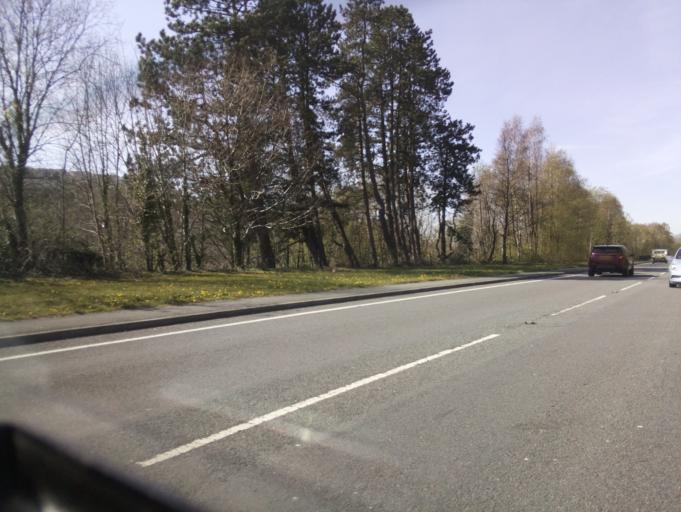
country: GB
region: Wales
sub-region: Rhondda Cynon Taf
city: Mountain Ash
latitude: 51.6695
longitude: -3.3574
